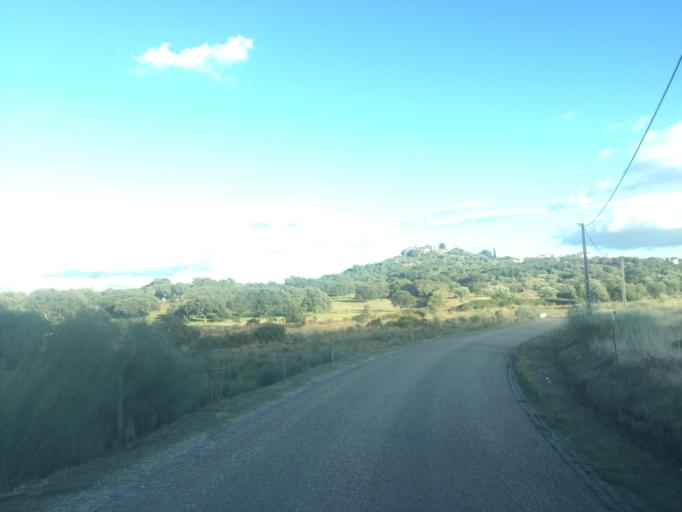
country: PT
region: Portalegre
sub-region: Alter do Chao
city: Alter do Chao
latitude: 39.1905
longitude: -7.6313
